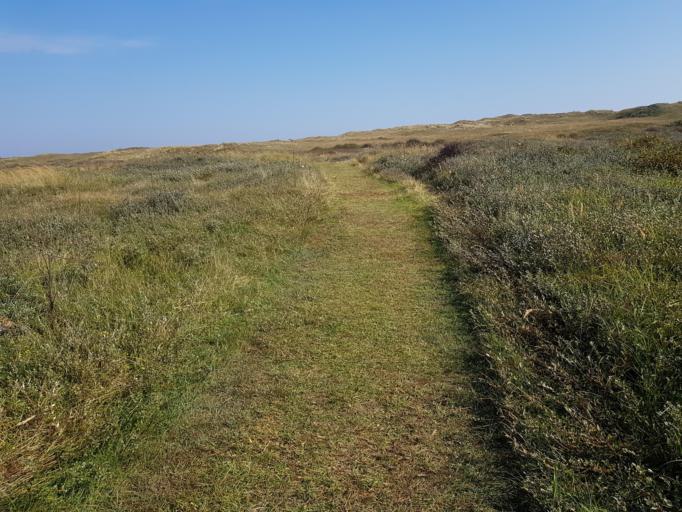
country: NL
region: North Holland
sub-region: Gemeente Texel
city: Den Burg
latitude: 53.1701
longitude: 4.8338
